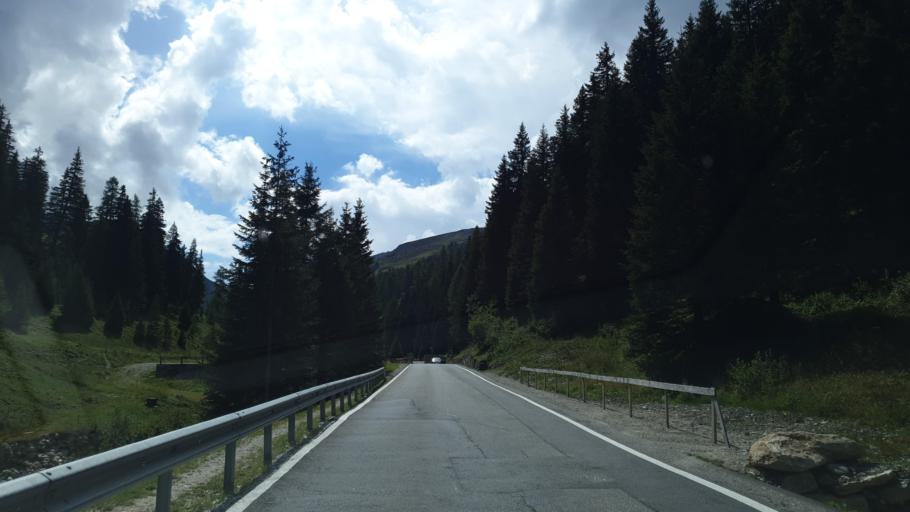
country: CH
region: Grisons
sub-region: Hinterrhein District
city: Hinterrhein
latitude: 46.5357
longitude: 9.3264
